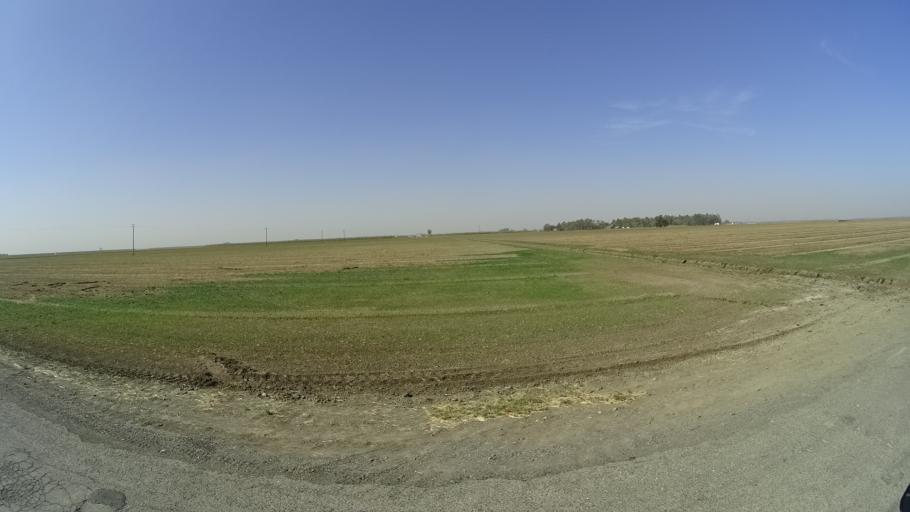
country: US
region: California
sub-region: Yolo County
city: Davis
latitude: 38.4714
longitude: -121.6936
